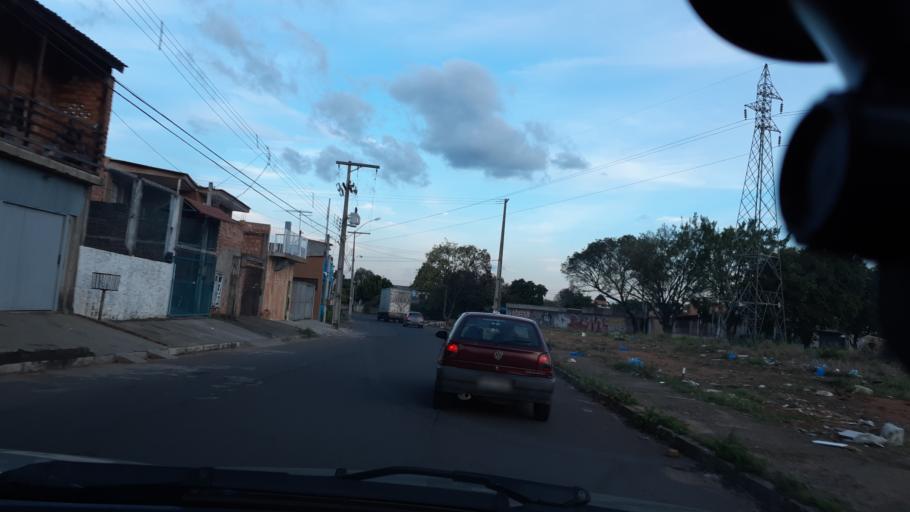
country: BR
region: Rio Grande do Sul
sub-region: Sapucaia Do Sul
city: Sapucaia
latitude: -29.8412
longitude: -51.1542
